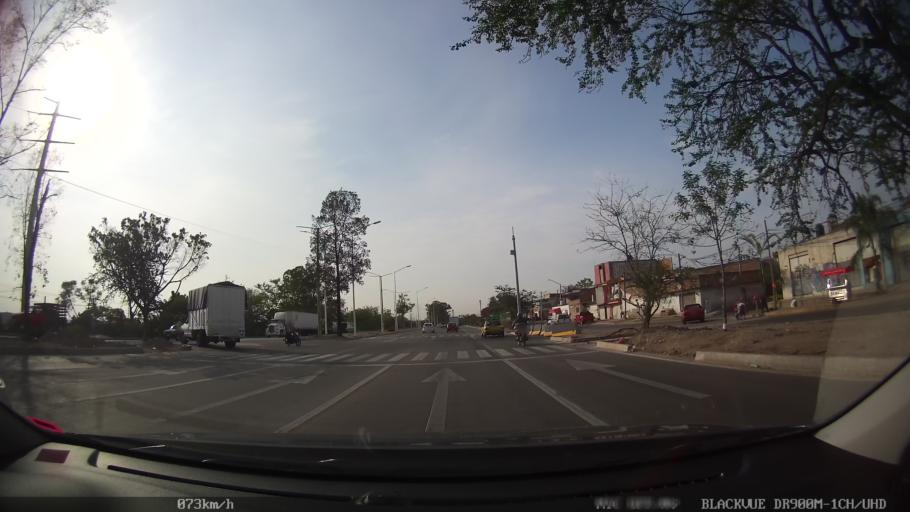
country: MX
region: Jalisco
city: Tlaquepaque
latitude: 20.7004
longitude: -103.2786
